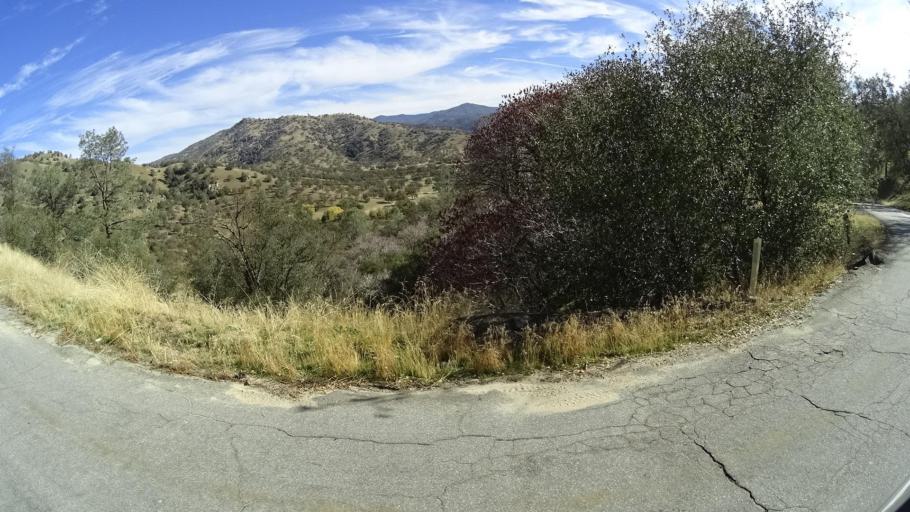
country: US
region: California
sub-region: Kern County
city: Alta Sierra
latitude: 35.6300
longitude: -118.7588
